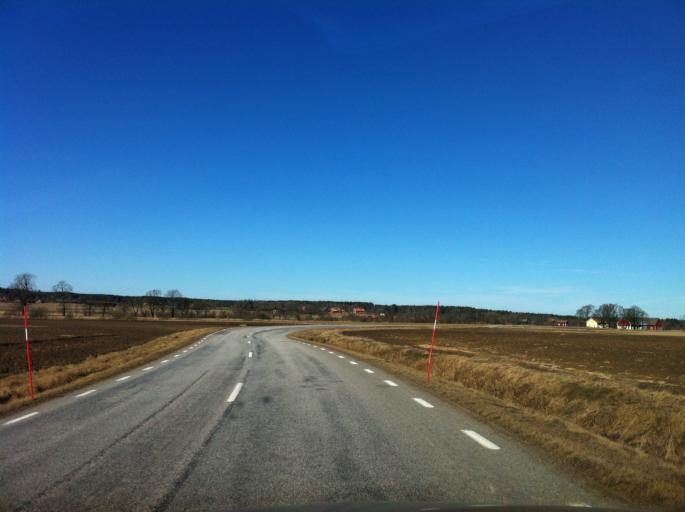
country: SE
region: Vaestra Goetaland
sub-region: Toreboda Kommun
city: Toereboda
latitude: 58.7051
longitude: 14.1269
